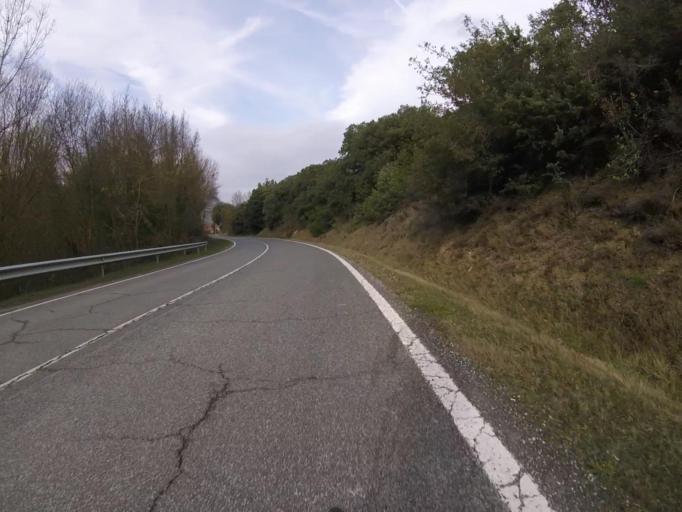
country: ES
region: Navarre
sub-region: Provincia de Navarra
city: Estella
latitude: 42.7068
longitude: -2.0684
